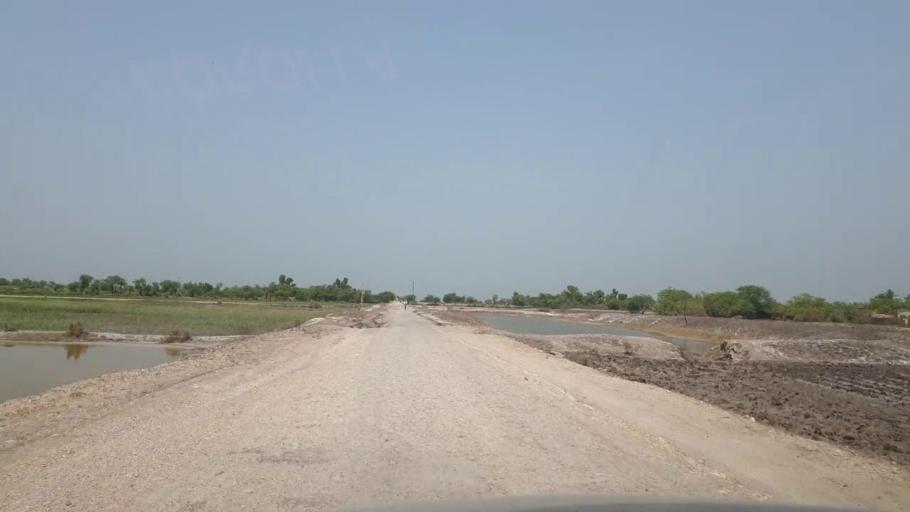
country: PK
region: Sindh
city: Garhi Yasin
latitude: 27.8746
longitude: 68.4461
